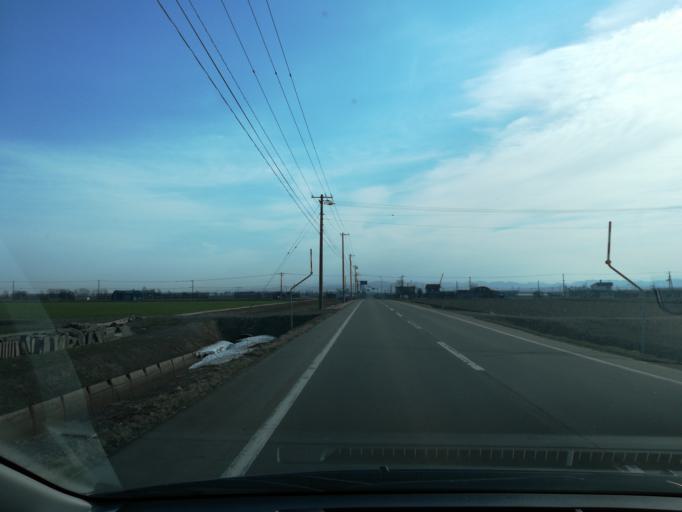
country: JP
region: Hokkaido
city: Iwamizawa
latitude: 43.1850
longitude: 141.6968
